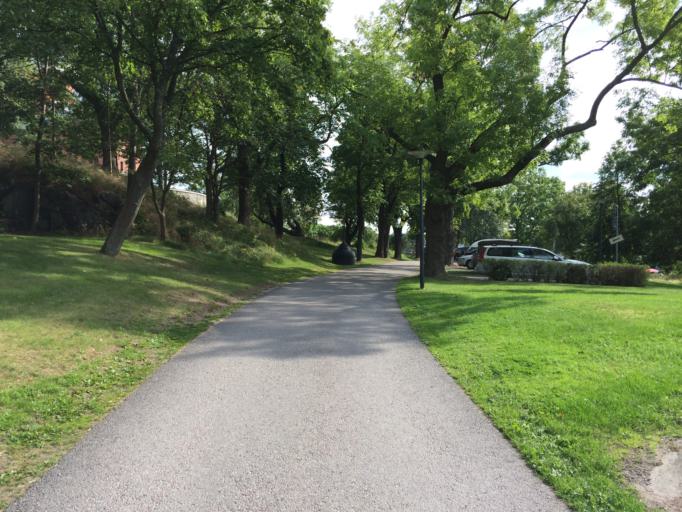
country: SE
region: Stockholm
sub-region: Stockholms Kommun
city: OEstermalm
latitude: 59.3229
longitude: 18.0887
